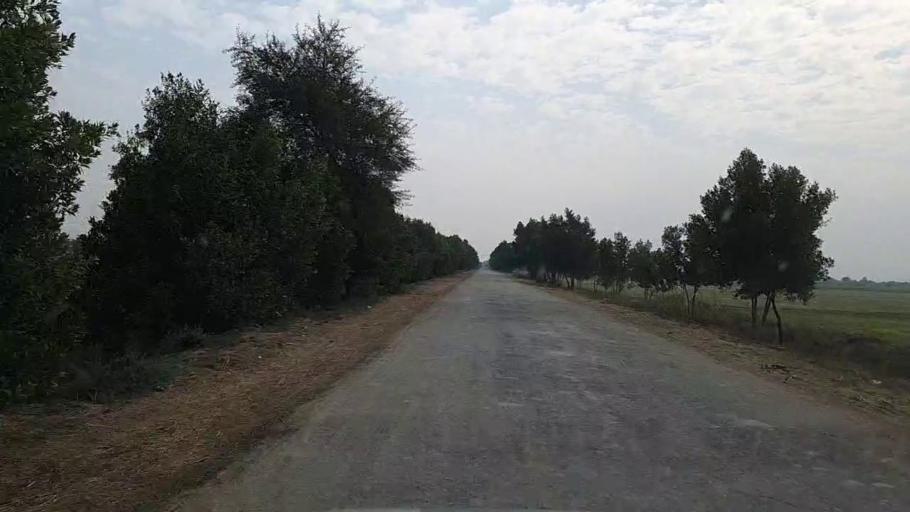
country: PK
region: Sindh
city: Mirwah Gorchani
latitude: 25.3797
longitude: 69.0818
